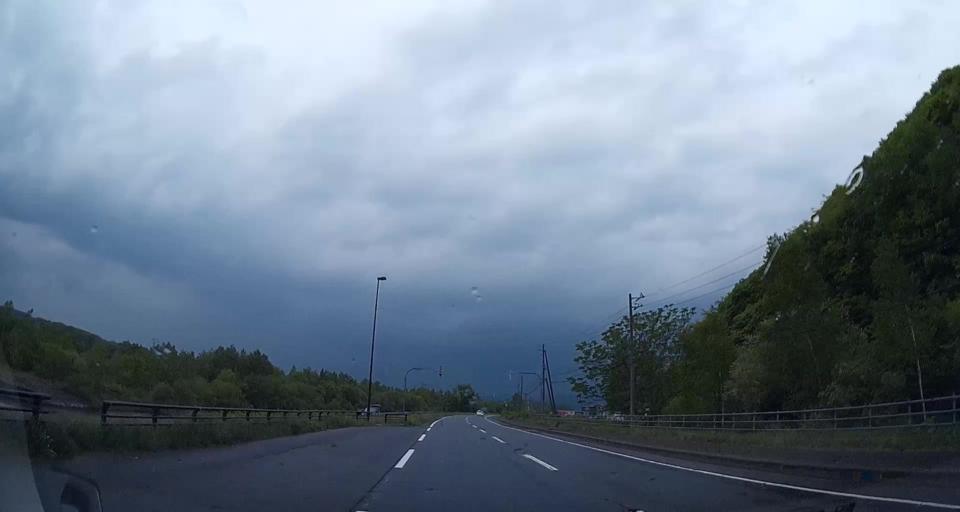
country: JP
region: Hokkaido
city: Niseko Town
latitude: 42.8382
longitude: 140.8914
